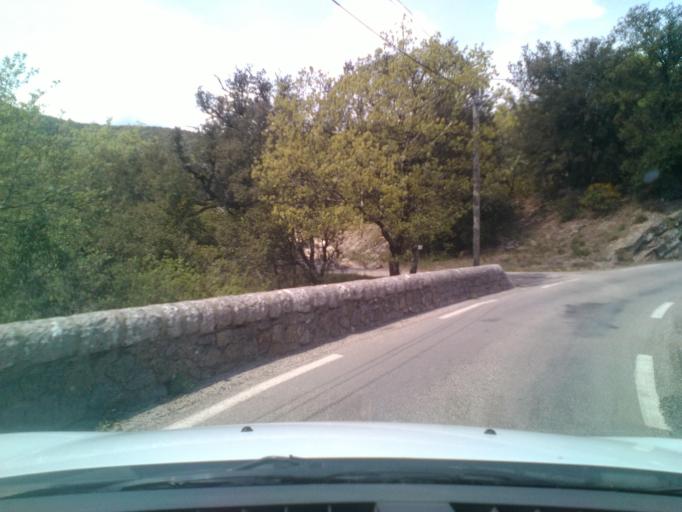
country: FR
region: Languedoc-Roussillon
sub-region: Departement du Gard
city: Saint-Hippolyte-du-Fort
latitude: 43.9871
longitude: 3.8803
